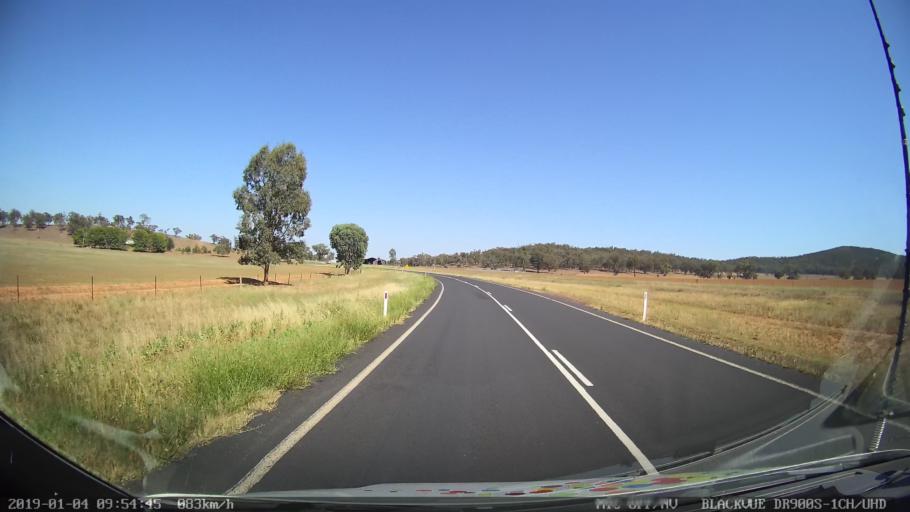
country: AU
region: New South Wales
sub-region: Cabonne
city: Canowindra
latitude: -33.5387
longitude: 148.4114
